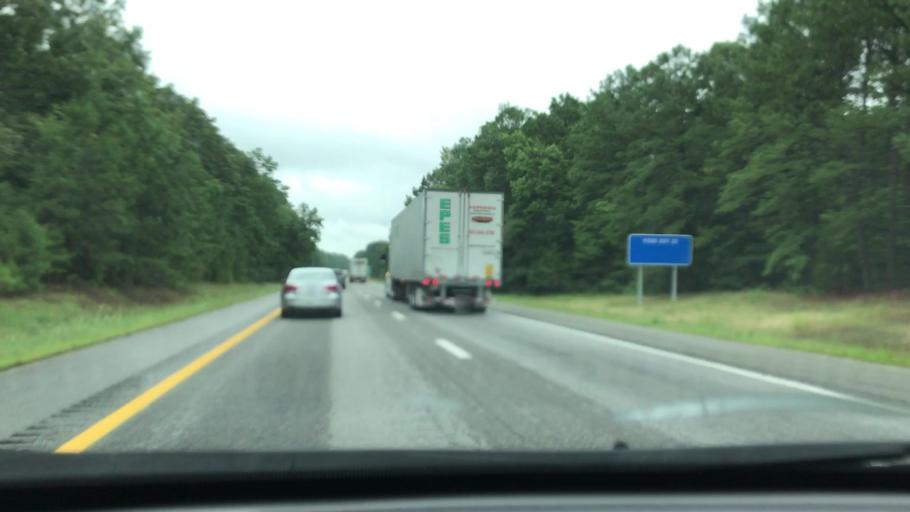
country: US
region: Virginia
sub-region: City of Emporia
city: Emporia
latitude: 36.7830
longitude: -77.4618
